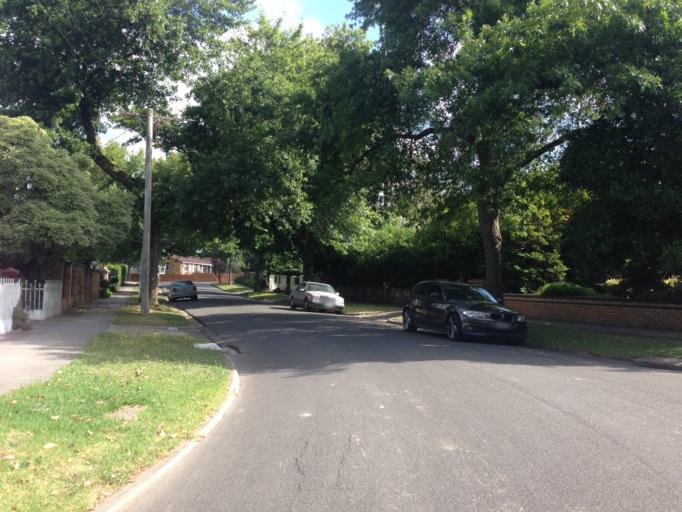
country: AU
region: Victoria
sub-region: Boroondara
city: Balwyn North
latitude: -37.7961
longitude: 145.0873
